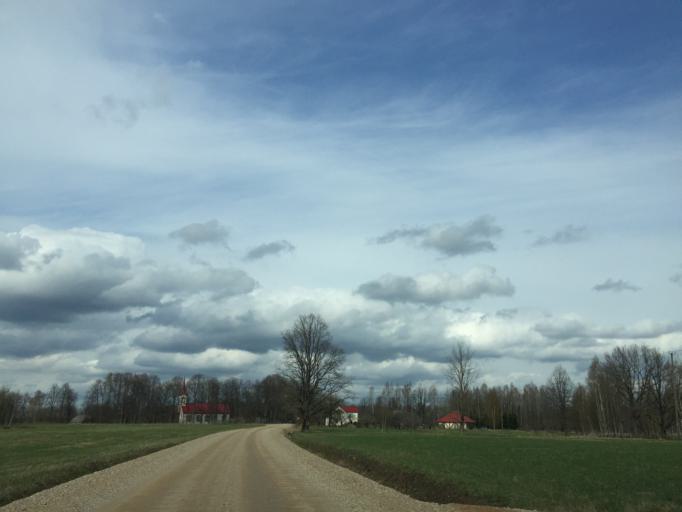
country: LV
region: Ligatne
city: Ligatne
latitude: 57.2140
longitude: 25.0680
